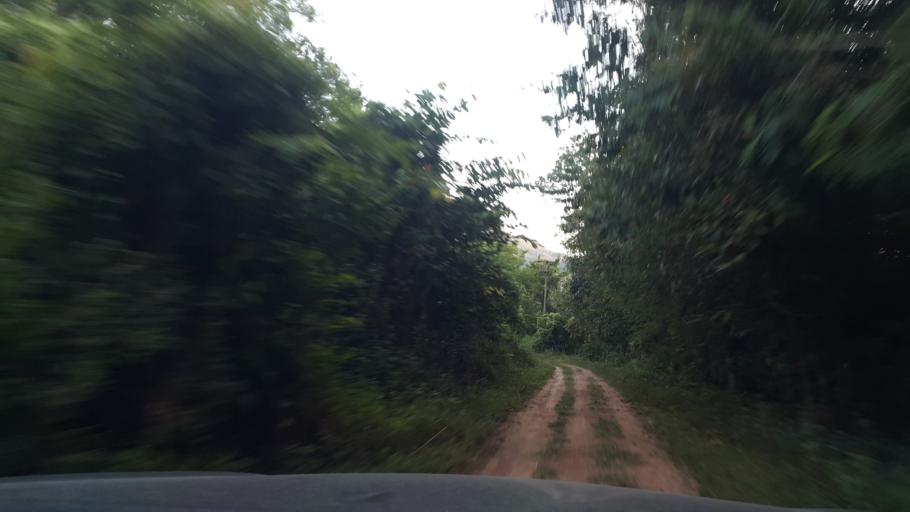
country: TH
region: Chiang Mai
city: San Kamphaeng
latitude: 18.6902
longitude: 99.2014
